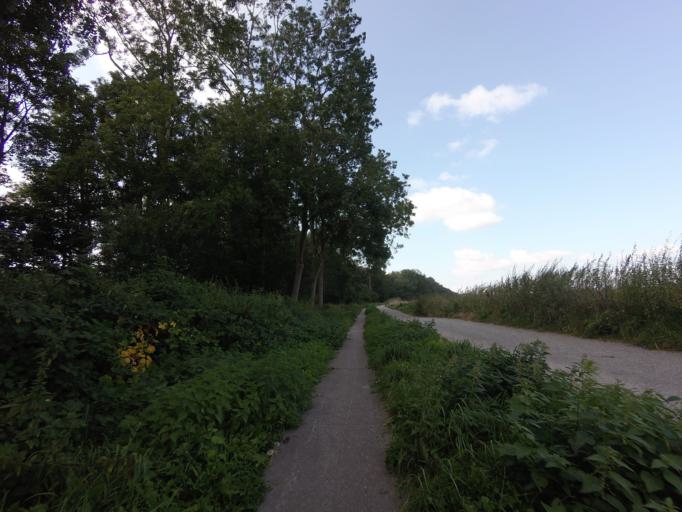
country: NL
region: Flevoland
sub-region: Gemeente Noordoostpolder
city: Ens
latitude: 52.6241
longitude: 5.7694
